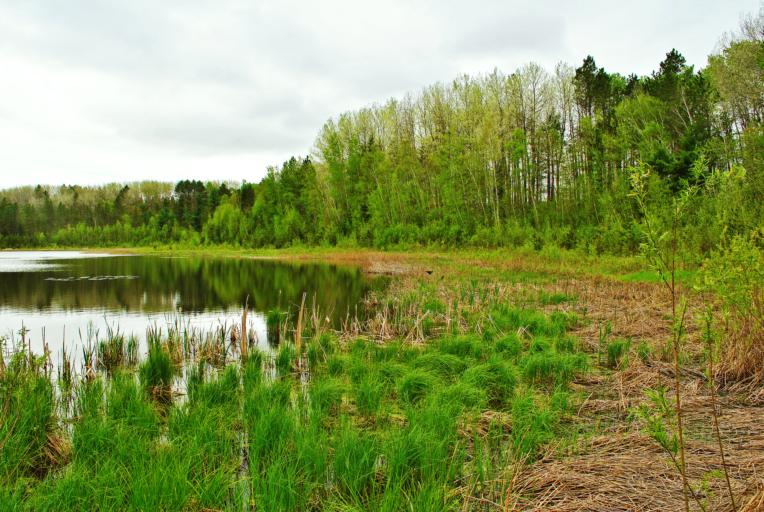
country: US
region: Wisconsin
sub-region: Douglas County
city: Lake Nebagamon
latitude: 46.4907
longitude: -91.5557
